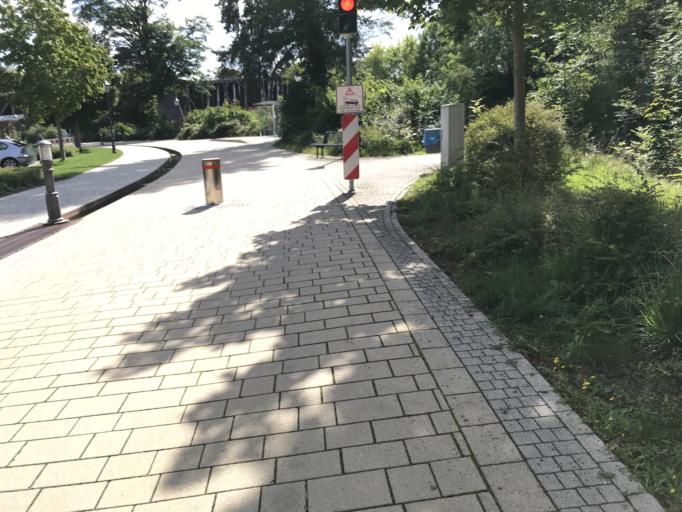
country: DE
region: Hesse
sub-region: Regierungsbezirk Kassel
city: Bad Sooden-Allendorf
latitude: 51.2709
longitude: 9.9651
